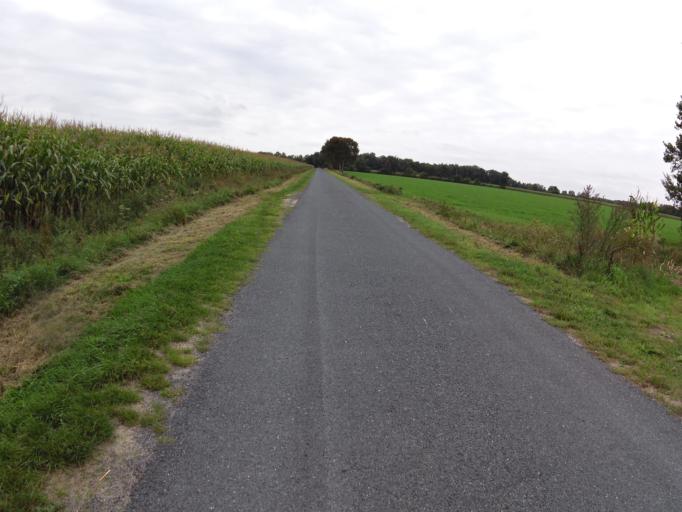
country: DE
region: Lower Saxony
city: Bad Bentheim
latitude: 52.2692
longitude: 7.1199
